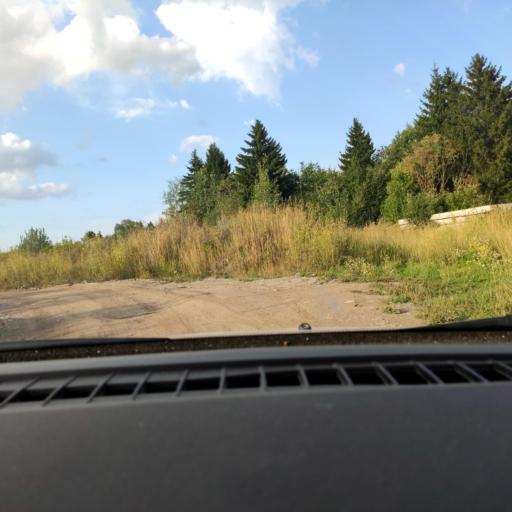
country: RU
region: Perm
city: Froly
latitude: 57.9308
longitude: 56.2848
